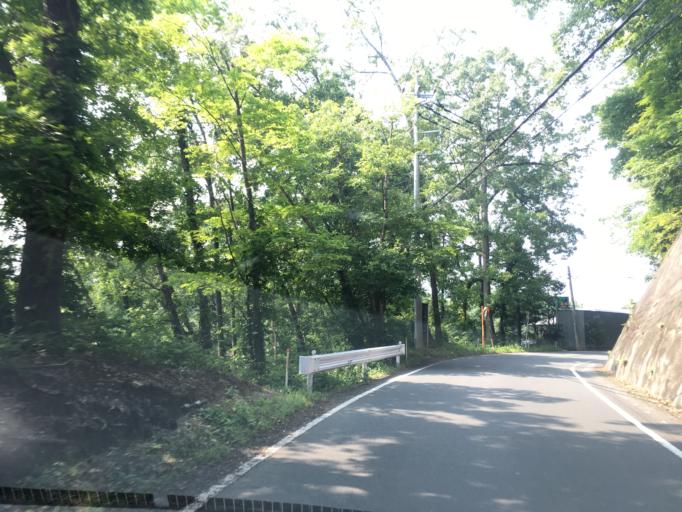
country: JP
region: Saitama
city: Chichibu
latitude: 36.0078
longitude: 139.1077
